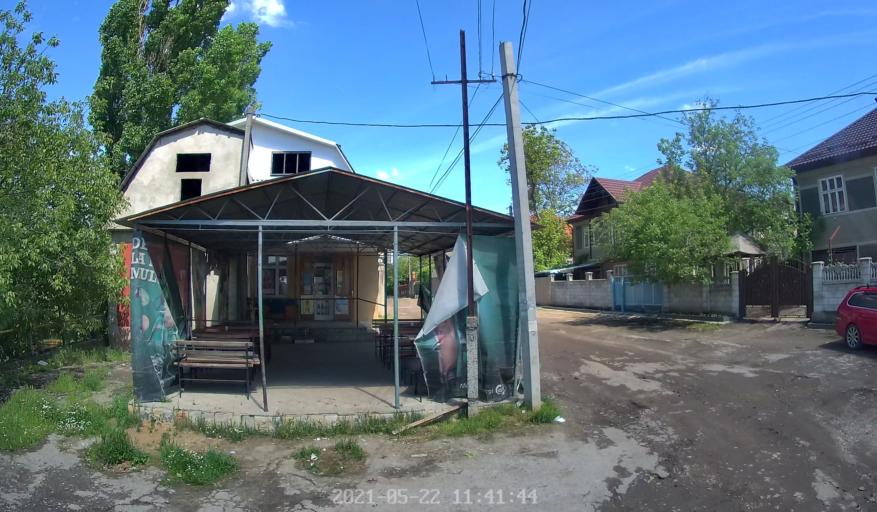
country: MD
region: Chisinau
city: Stauceni
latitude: 47.0979
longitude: 28.8288
